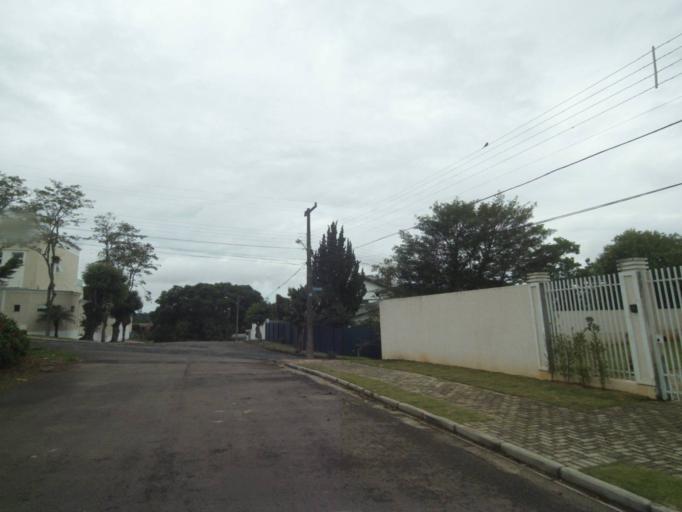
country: BR
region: Parana
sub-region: Curitiba
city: Curitiba
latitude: -25.4282
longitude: -49.3161
